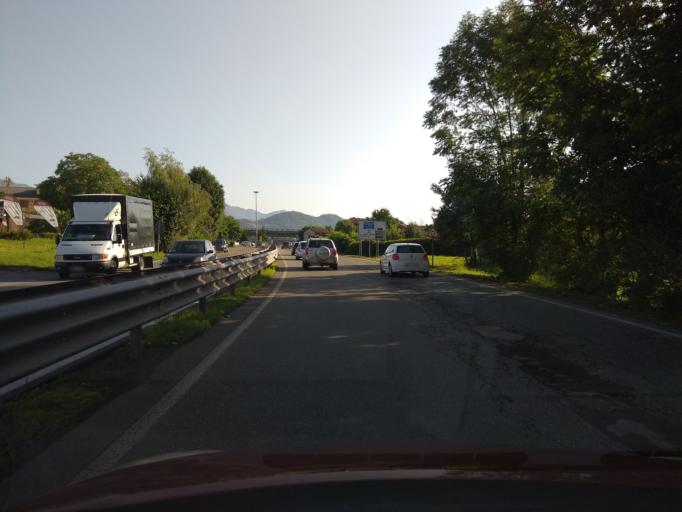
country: IT
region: Piedmont
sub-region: Provincia di Biella
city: Gaglianico
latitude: 45.5518
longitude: 8.0721
